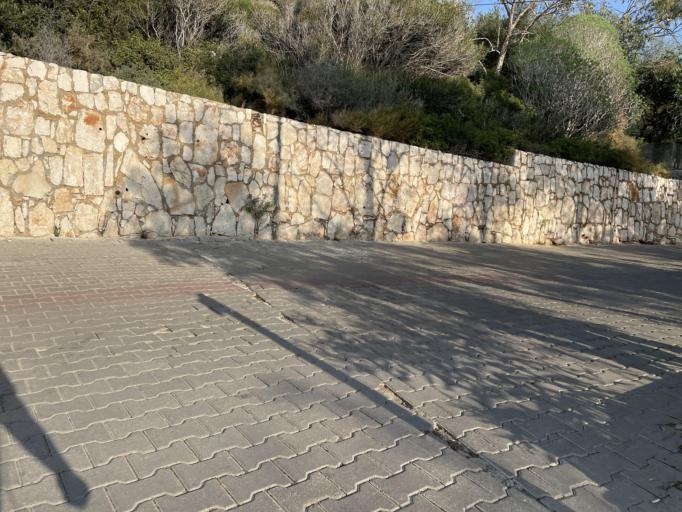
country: TR
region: Antalya
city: Kas
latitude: 36.1959
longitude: 29.6463
